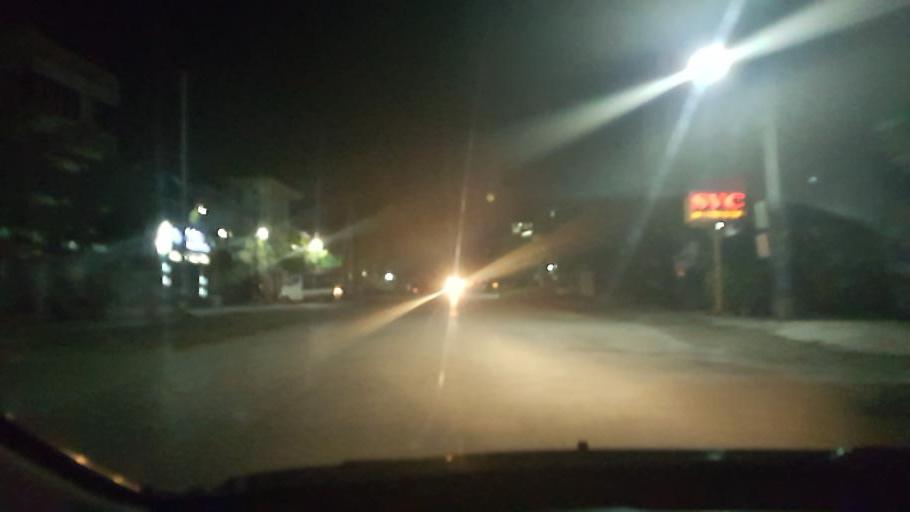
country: MM
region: Mandalay
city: Mandalay
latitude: 21.9812
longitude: 96.0929
